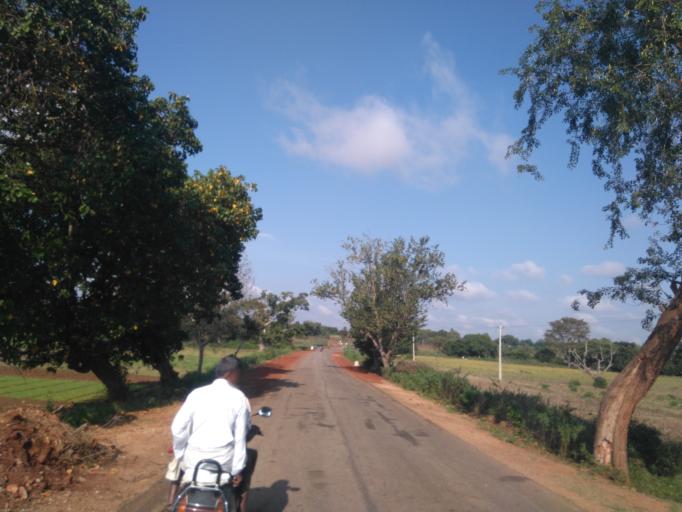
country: IN
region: Karnataka
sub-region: Mandya
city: Malavalli
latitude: 12.2653
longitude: 77.0228
